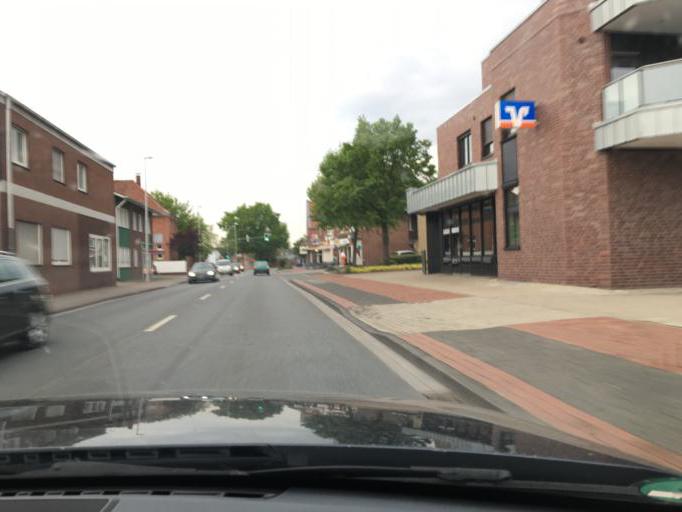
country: DE
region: North Rhine-Westphalia
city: Emsdetten
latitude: 52.1710
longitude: 7.5390
